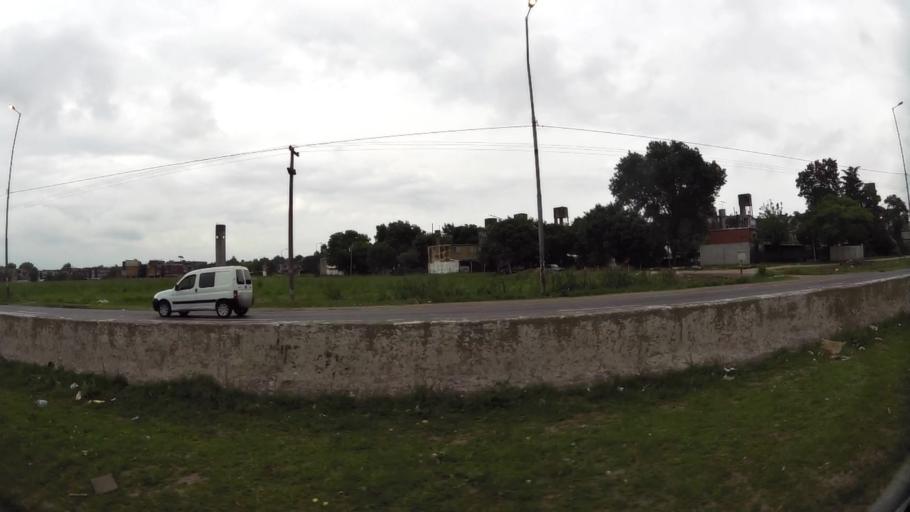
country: AR
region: Buenos Aires
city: San Justo
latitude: -34.7036
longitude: -58.5365
